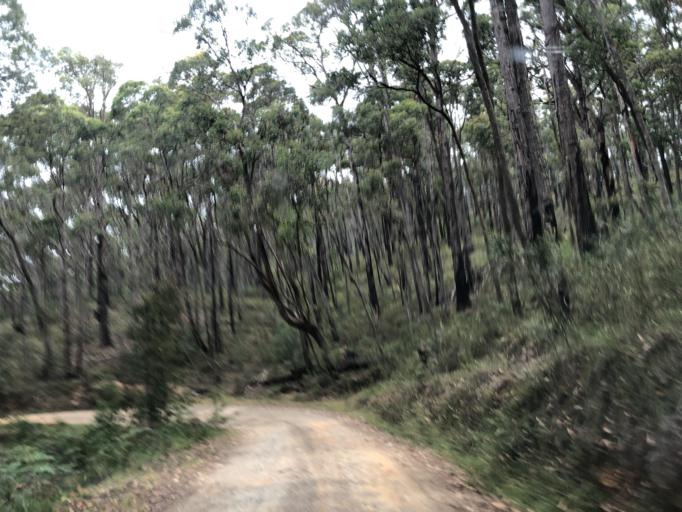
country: AU
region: Victoria
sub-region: Moorabool
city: Bacchus Marsh
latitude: -37.4750
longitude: 144.2843
